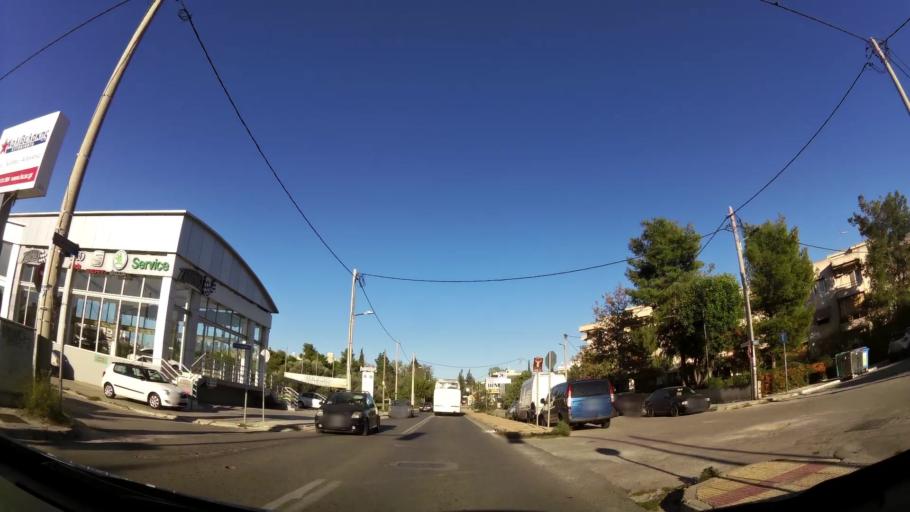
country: GR
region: Attica
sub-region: Nomarchia Athinas
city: Lykovrysi
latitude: 38.0718
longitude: 23.7868
